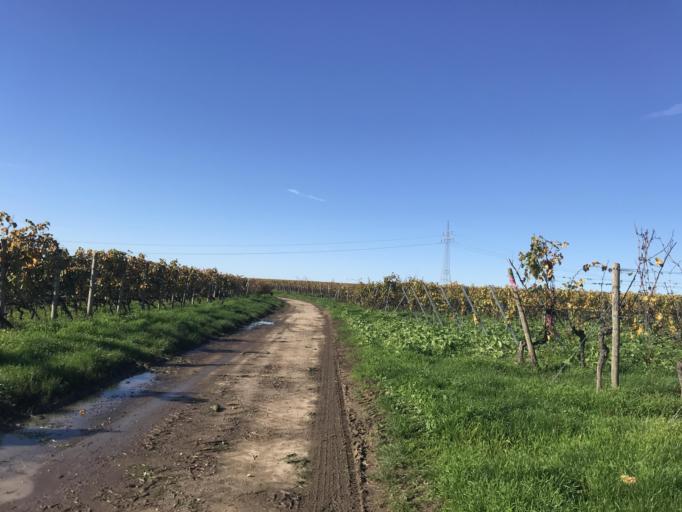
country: DE
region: Hesse
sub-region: Regierungsbezirk Darmstadt
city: Hochheim am Main
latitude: 50.0110
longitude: 8.3345
